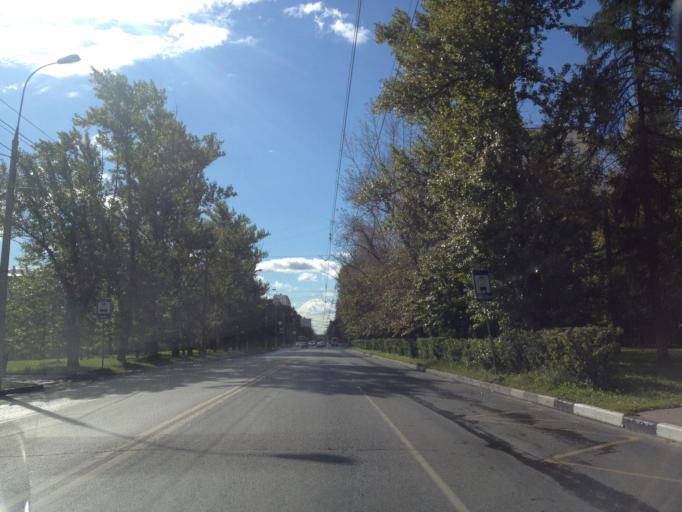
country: RU
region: Moscow
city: Metrogorodok
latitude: 55.8049
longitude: 37.7988
